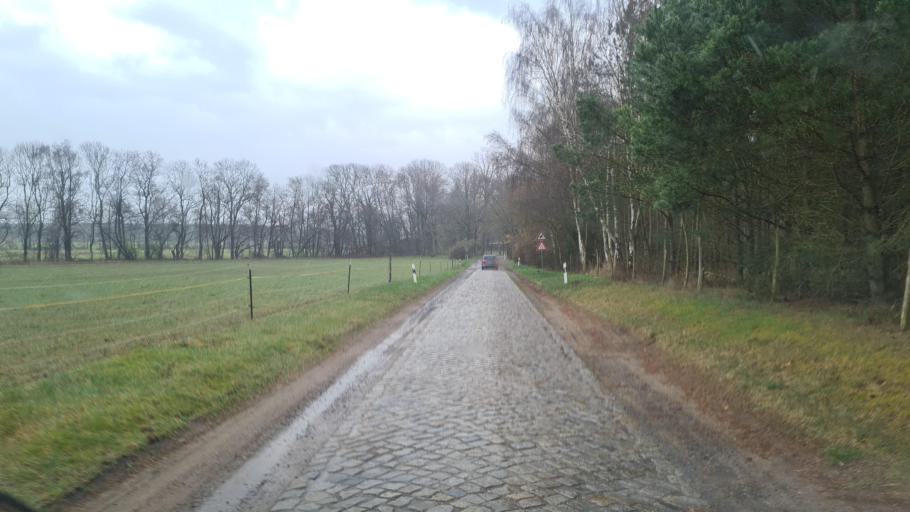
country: DE
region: Brandenburg
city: Linthe
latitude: 52.1533
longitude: 12.7179
